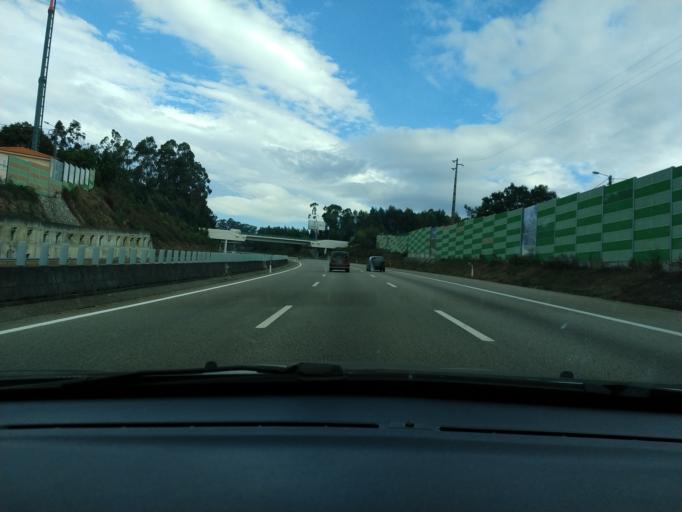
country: PT
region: Aveiro
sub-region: Santa Maria da Feira
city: Rio Meao
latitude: 40.9593
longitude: -8.5687
